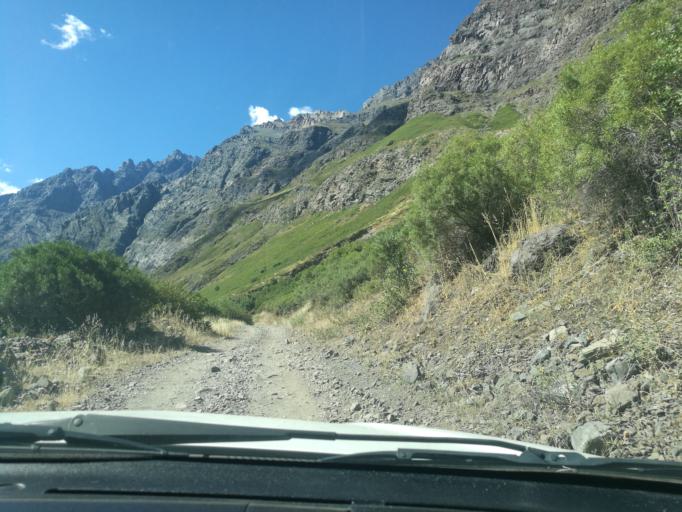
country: CL
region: O'Higgins
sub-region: Provincia de Cachapoal
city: Machali
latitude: -34.3837
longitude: -70.2830
